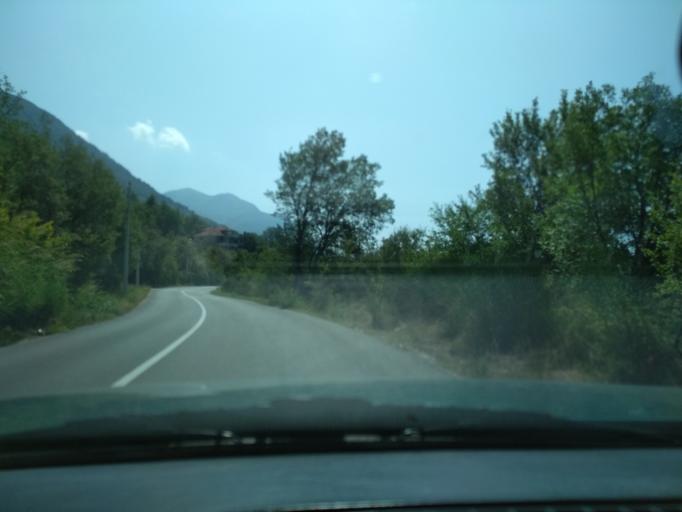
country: ME
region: Kotor
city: Kotor
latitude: 42.3924
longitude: 18.7561
